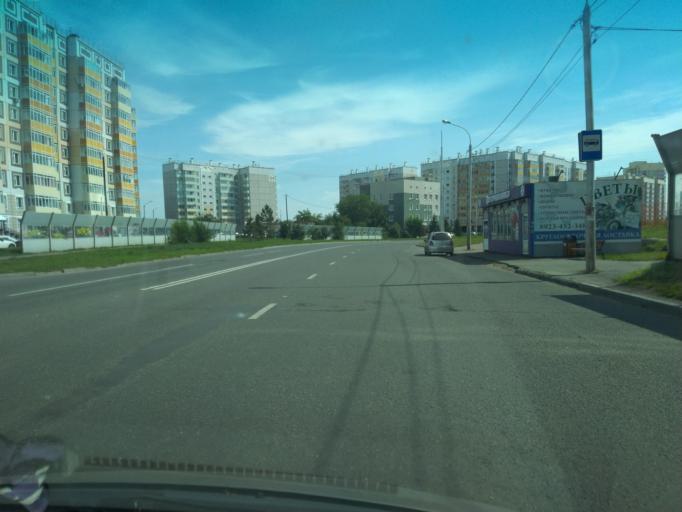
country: RU
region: Krasnoyarskiy
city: Solnechnyy
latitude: 56.0538
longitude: 92.9211
